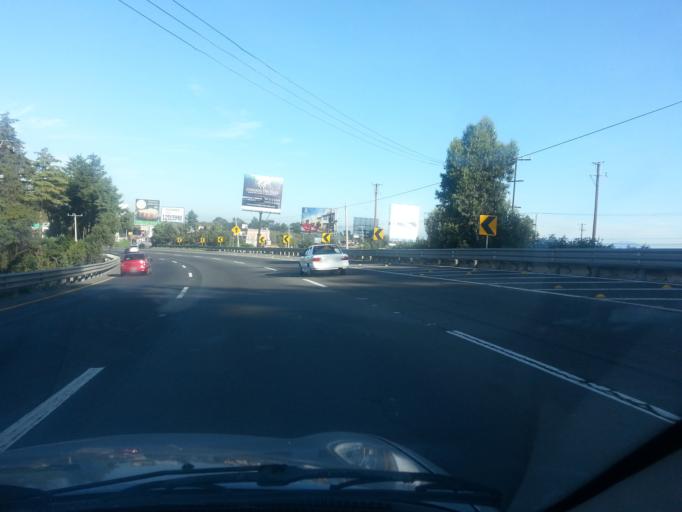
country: MX
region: Mexico
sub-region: Lerma
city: Fraccionamiento y Club de Golf los Encinos
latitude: 19.2846
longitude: -99.4883
